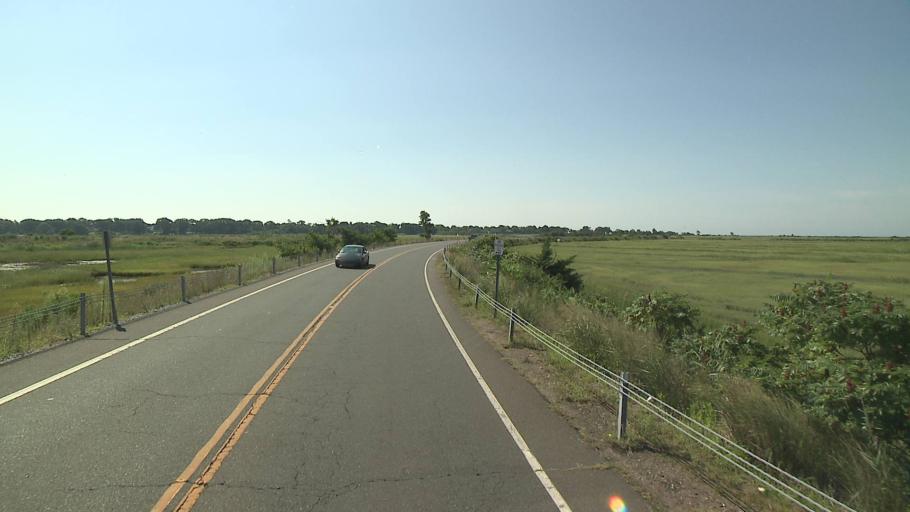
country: US
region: Connecticut
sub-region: Fairfield County
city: Stratford
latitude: 41.1616
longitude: -73.1337
